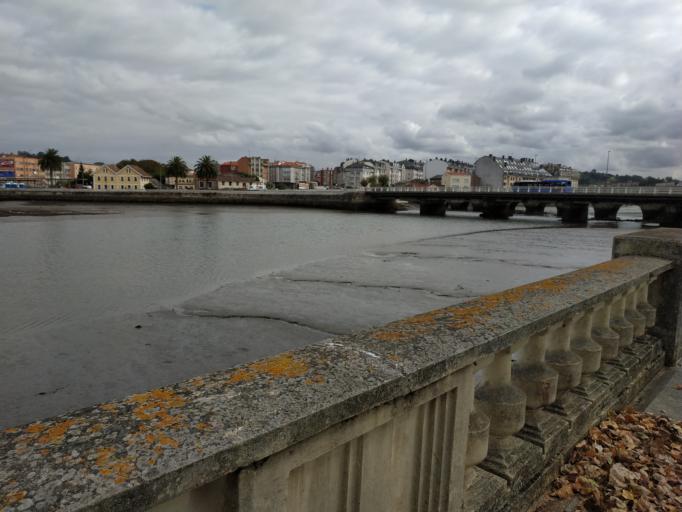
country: ES
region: Galicia
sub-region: Provincia da Coruna
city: Cambre
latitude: 43.3167
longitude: -8.3608
